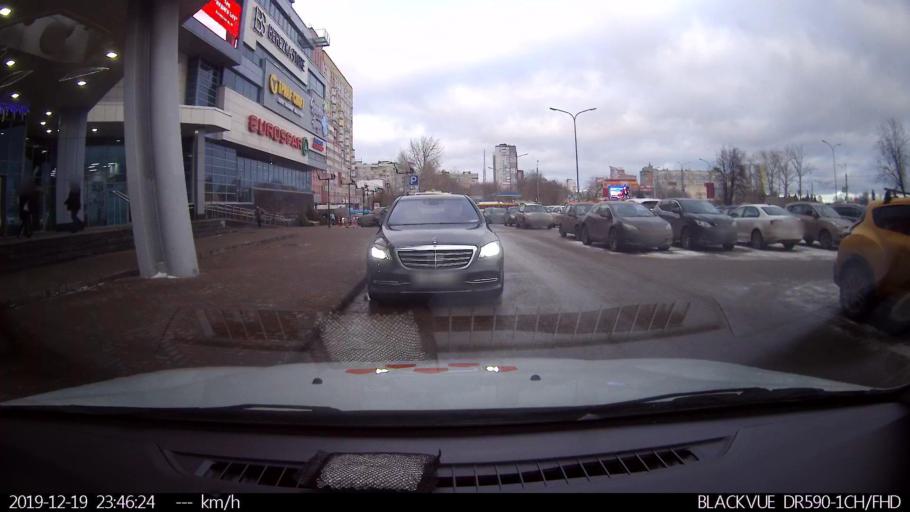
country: RU
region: Jaroslavl
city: Breytovo
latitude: 58.2083
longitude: 37.7299
